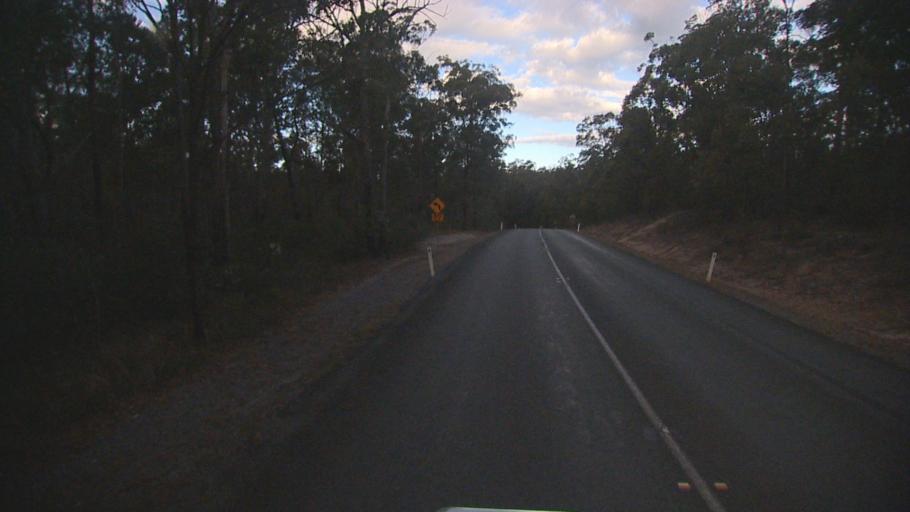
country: AU
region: Queensland
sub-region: Logan
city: Windaroo
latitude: -27.8073
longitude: 153.1471
